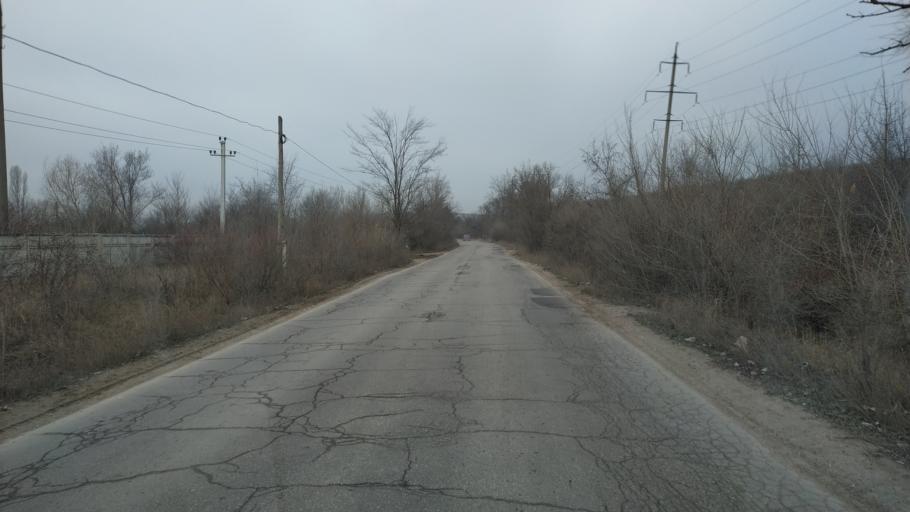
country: MD
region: Chisinau
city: Vatra
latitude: 47.0702
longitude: 28.7750
